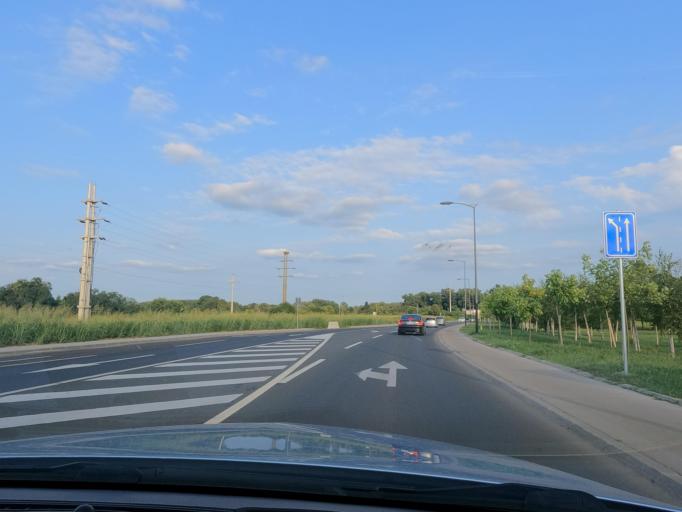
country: RS
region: Central Serbia
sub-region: Belgrade
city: Obrenovac
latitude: 44.6570
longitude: 20.2165
